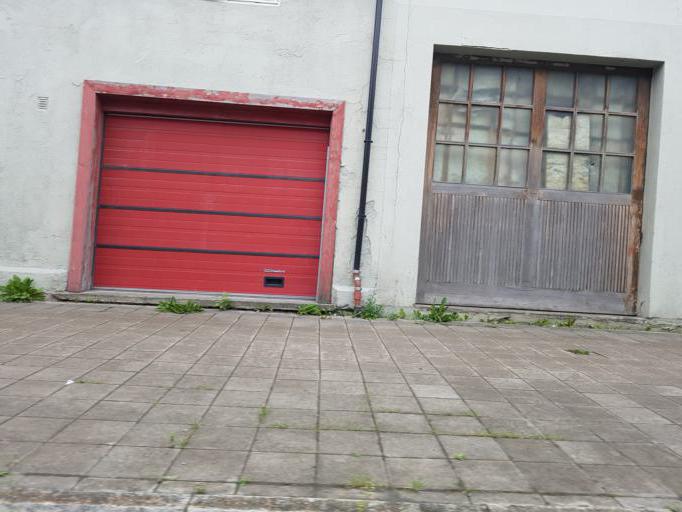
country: NO
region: Nord-Trondelag
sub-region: Levanger
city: Levanger
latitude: 63.7479
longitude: 11.3014
